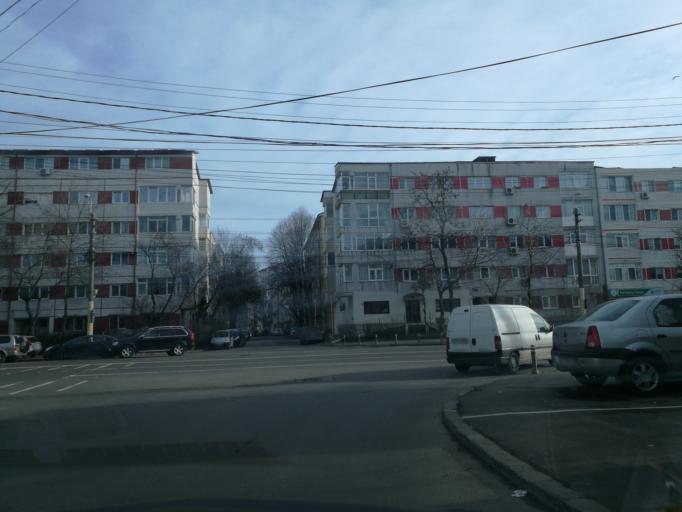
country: RO
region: Constanta
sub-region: Municipiul Constanta
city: Constanta
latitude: 44.1787
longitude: 28.6157
